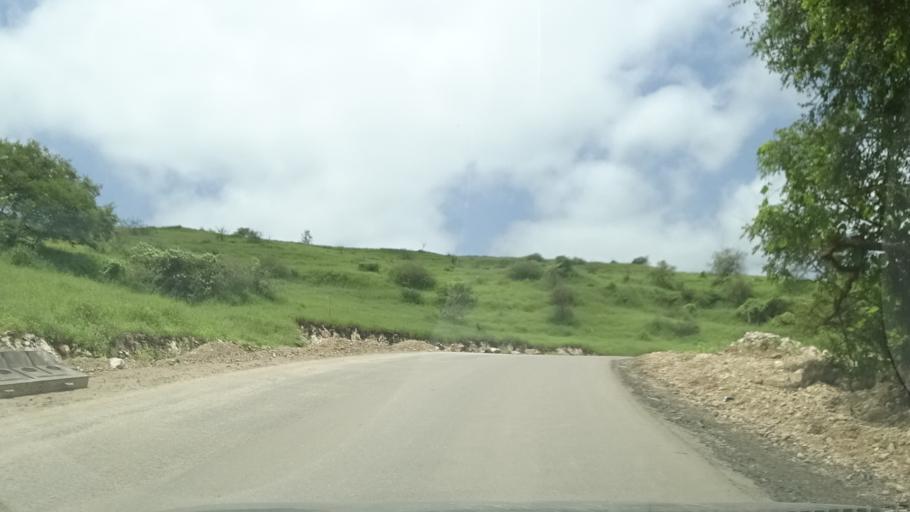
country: OM
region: Zufar
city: Salalah
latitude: 17.1797
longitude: 54.1599
